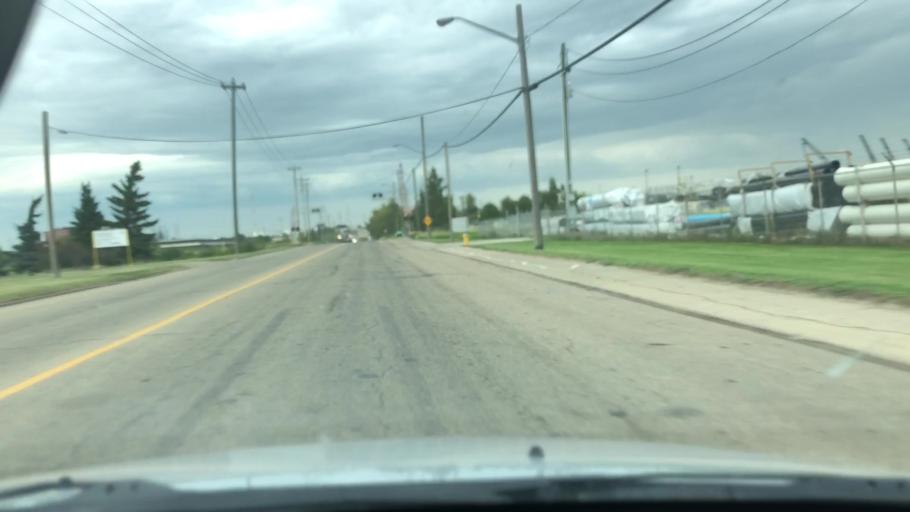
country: CA
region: Alberta
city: Edmonton
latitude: 53.5267
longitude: -113.4028
